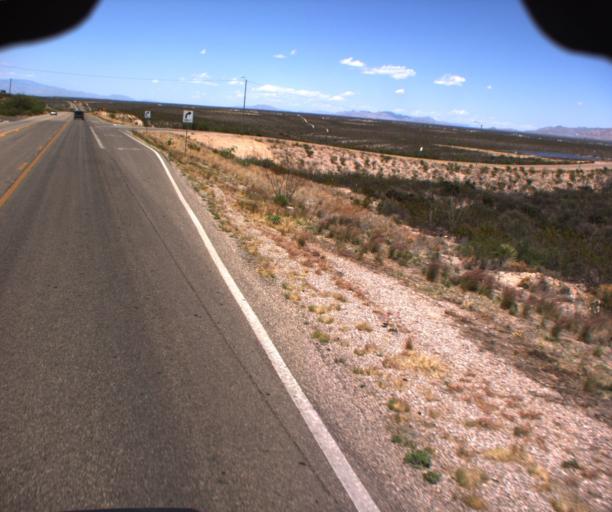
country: US
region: Arizona
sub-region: Cochise County
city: Tombstone
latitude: 31.7225
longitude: -110.0729
